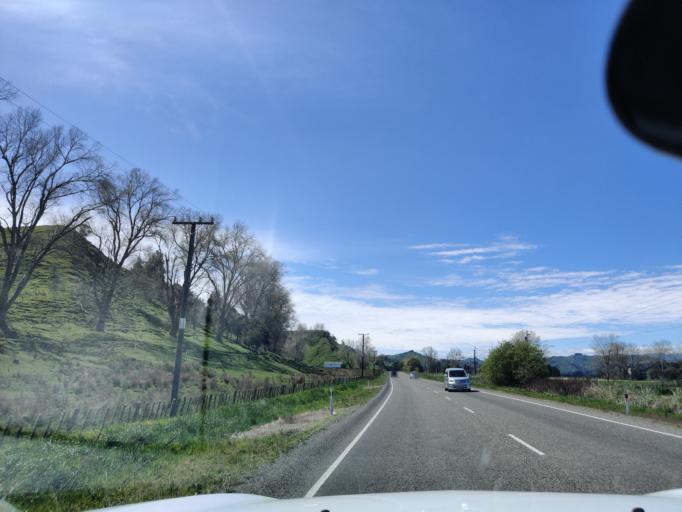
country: NZ
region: Manawatu-Wanganui
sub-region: Ruapehu District
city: Waiouru
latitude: -39.8543
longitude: 175.7270
